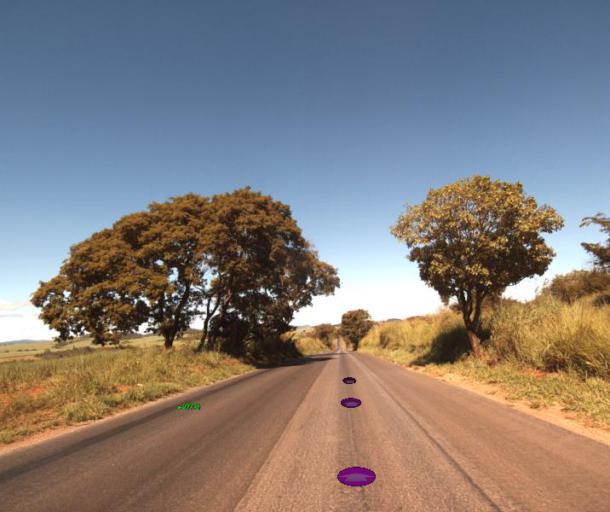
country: BR
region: Goias
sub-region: Itapaci
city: Itapaci
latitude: -15.1240
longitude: -49.5047
